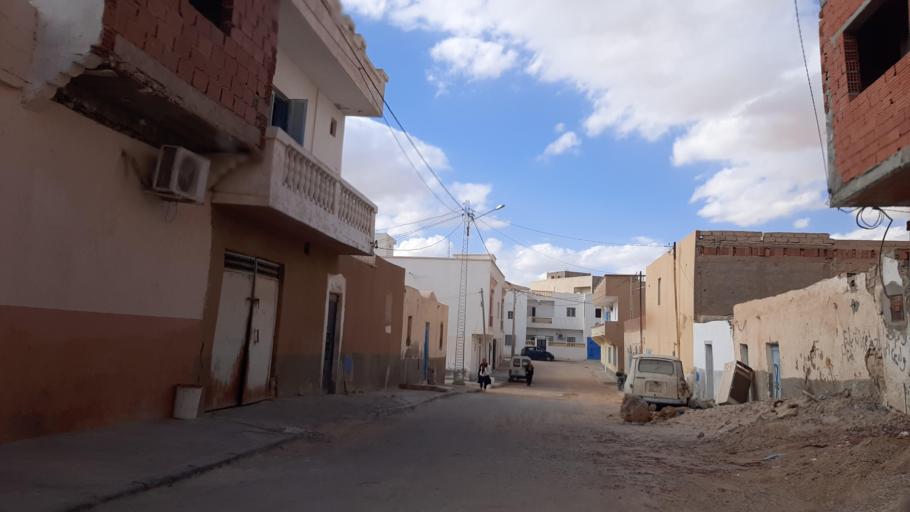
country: TN
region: Tataouine
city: Tataouine
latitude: 32.9311
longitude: 10.4551
